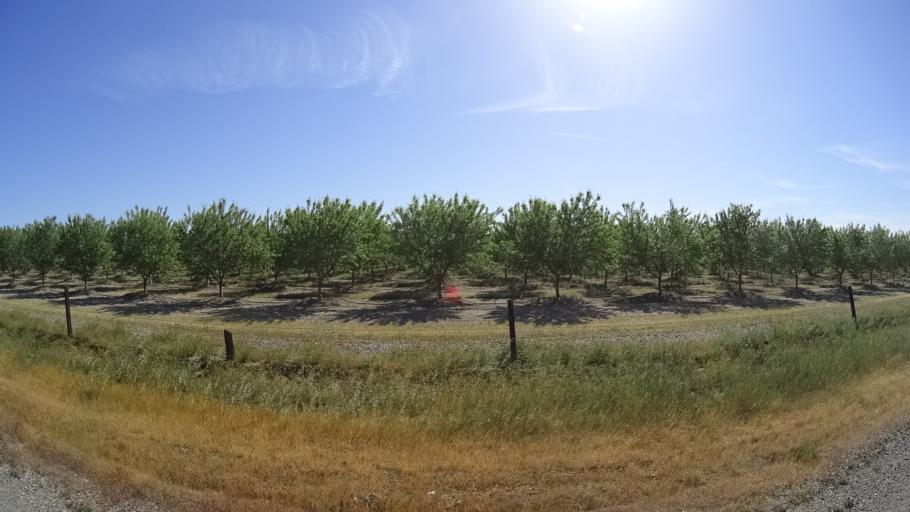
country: US
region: California
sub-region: Glenn County
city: Willows
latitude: 39.6285
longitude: -122.1600
